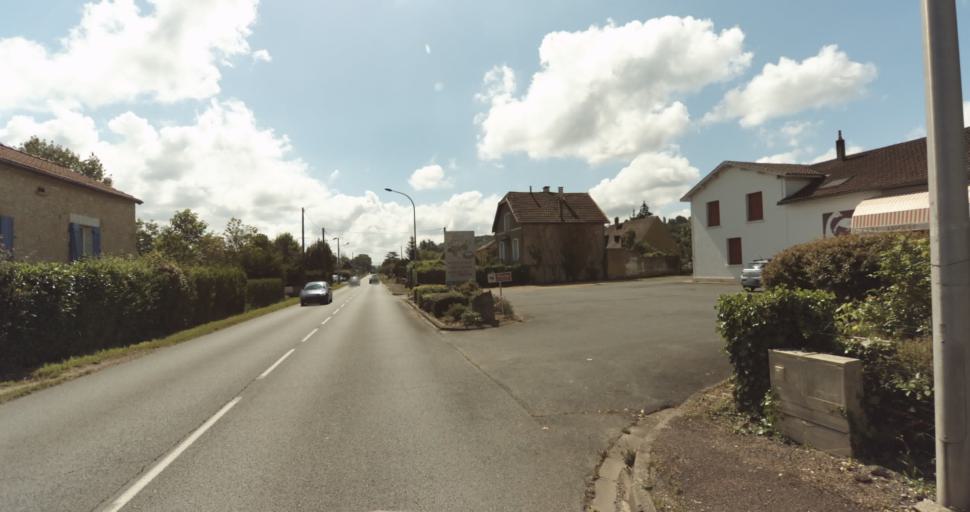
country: FR
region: Aquitaine
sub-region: Departement de la Dordogne
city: Le Bugue
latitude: 44.8455
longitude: 0.9177
